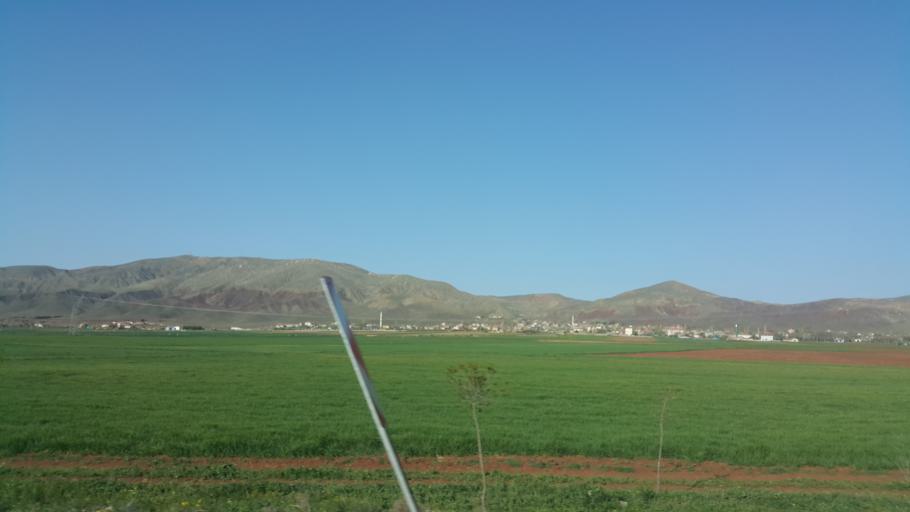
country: TR
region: Aksaray
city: Acipinar
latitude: 38.6098
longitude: 33.7655
